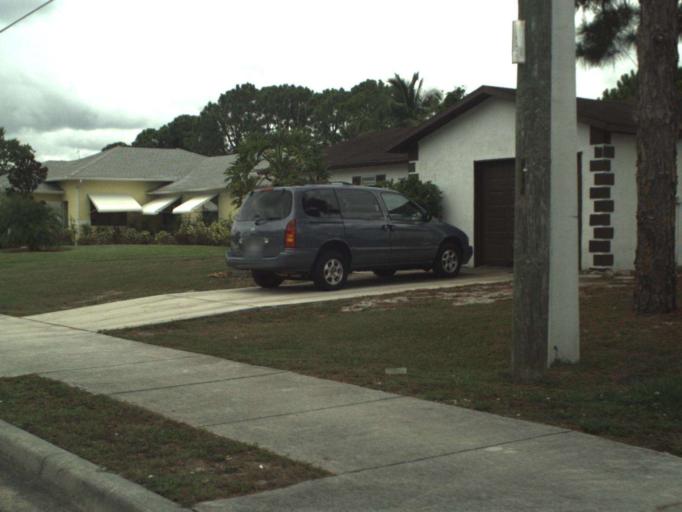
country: US
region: Florida
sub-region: Saint Lucie County
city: Port Saint Lucie
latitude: 27.2871
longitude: -80.3460
